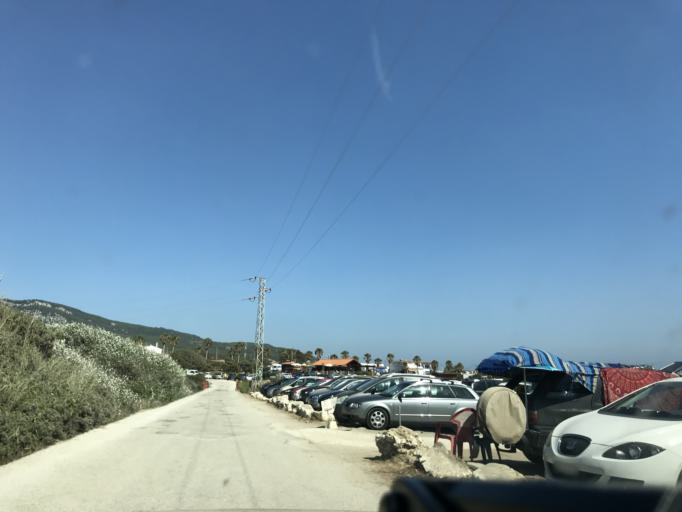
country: ES
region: Andalusia
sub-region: Provincia de Cadiz
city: Zahara de los Atunes
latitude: 36.0875
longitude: -5.7698
